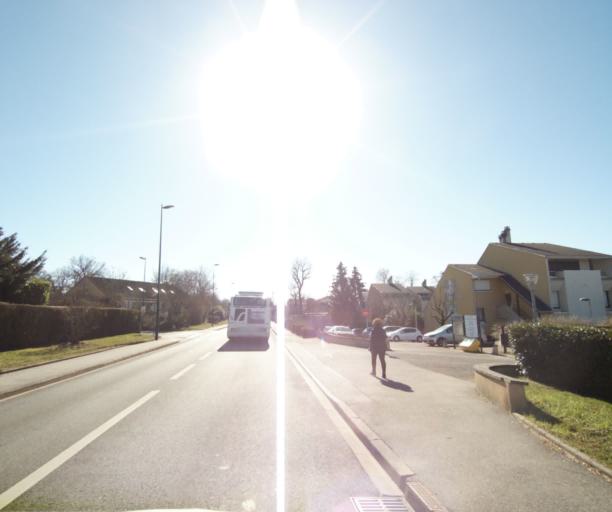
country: FR
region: Lorraine
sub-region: Departement de Meurthe-et-Moselle
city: Heillecourt
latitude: 48.6628
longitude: 6.2074
